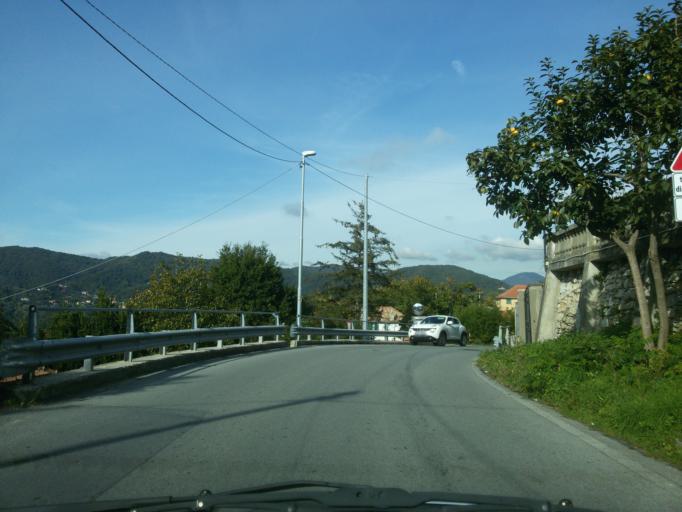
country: IT
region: Liguria
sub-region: Provincia di Genova
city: Piccarello
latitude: 44.4731
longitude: 8.9601
